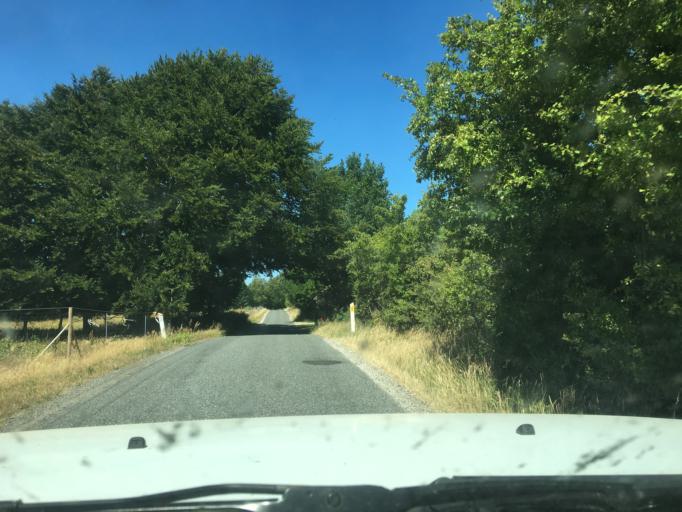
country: DK
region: Central Jutland
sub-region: Syddjurs Kommune
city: Ryomgard
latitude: 56.4817
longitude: 10.5939
